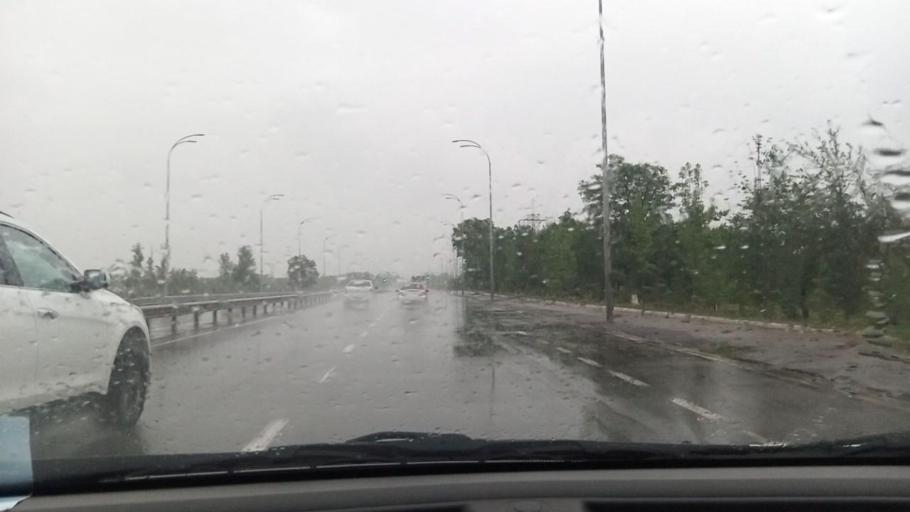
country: UZ
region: Toshkent Shahri
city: Bektemir
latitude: 41.2602
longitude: 69.3762
